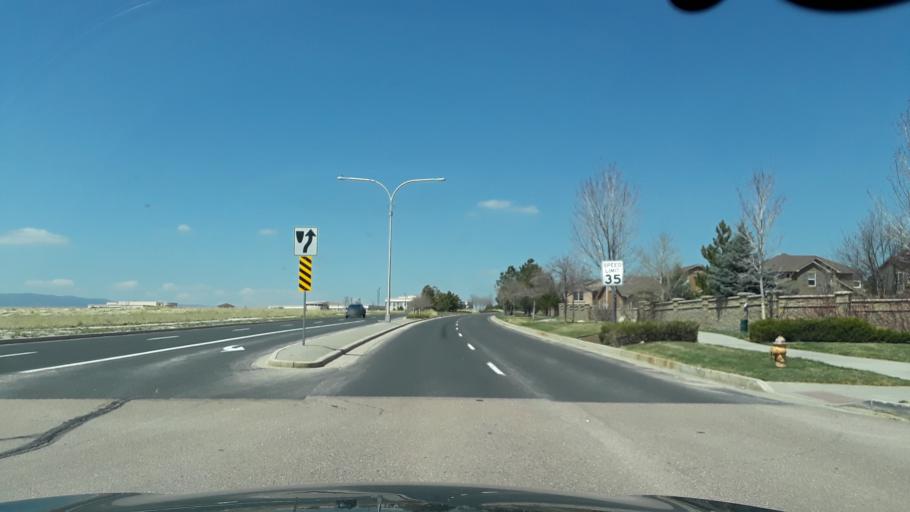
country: US
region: Colorado
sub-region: El Paso County
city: Black Forest
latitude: 38.9646
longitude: -104.7344
